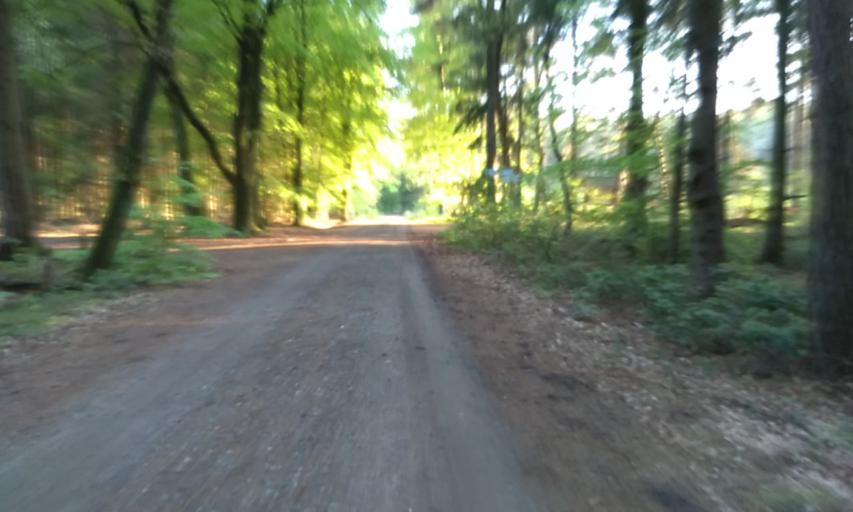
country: DE
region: Lower Saxony
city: Dollern
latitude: 53.5174
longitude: 9.5364
